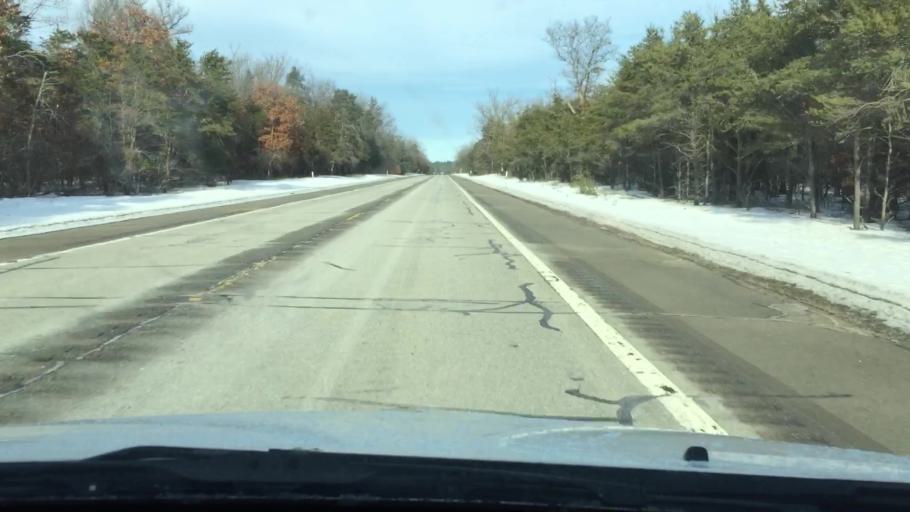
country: US
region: Michigan
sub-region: Wexford County
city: Manton
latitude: 44.5330
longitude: -85.3825
